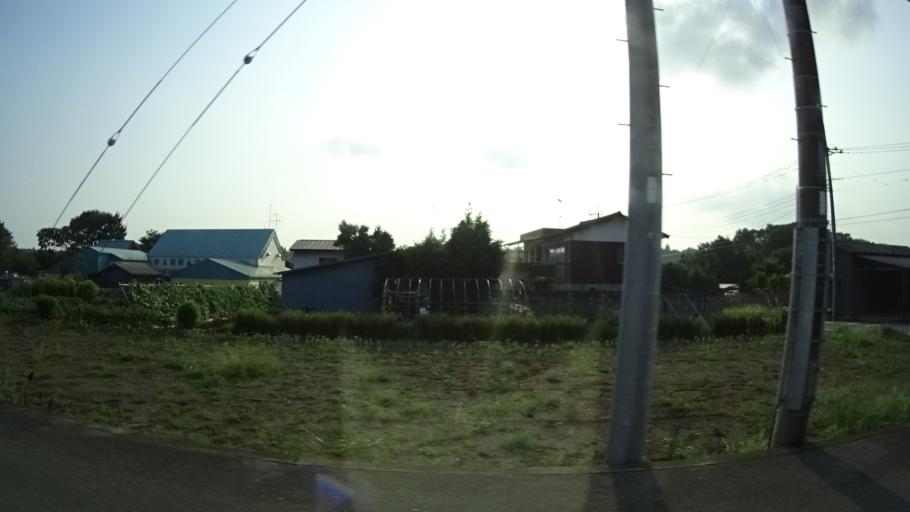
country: JP
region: Tochigi
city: Mashiko
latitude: 36.5469
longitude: 140.1034
